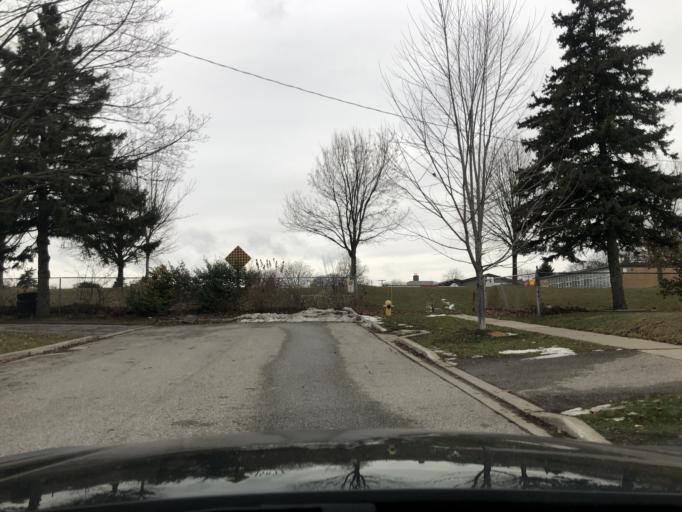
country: CA
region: Ontario
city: Etobicoke
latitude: 43.6942
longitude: -79.5370
